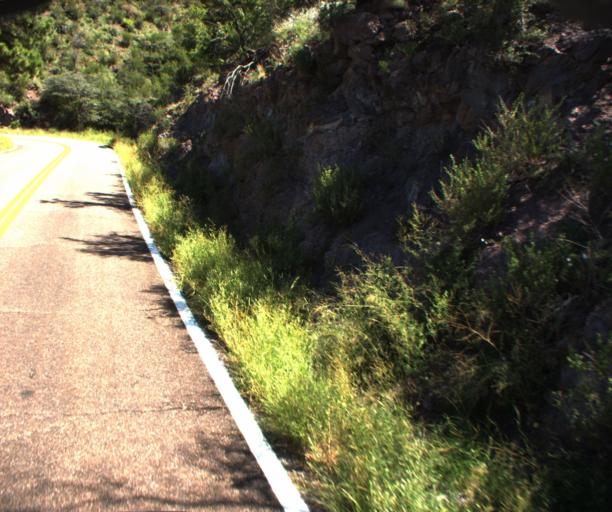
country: US
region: Arizona
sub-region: Greenlee County
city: Morenci
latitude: 33.2246
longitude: -109.3886
